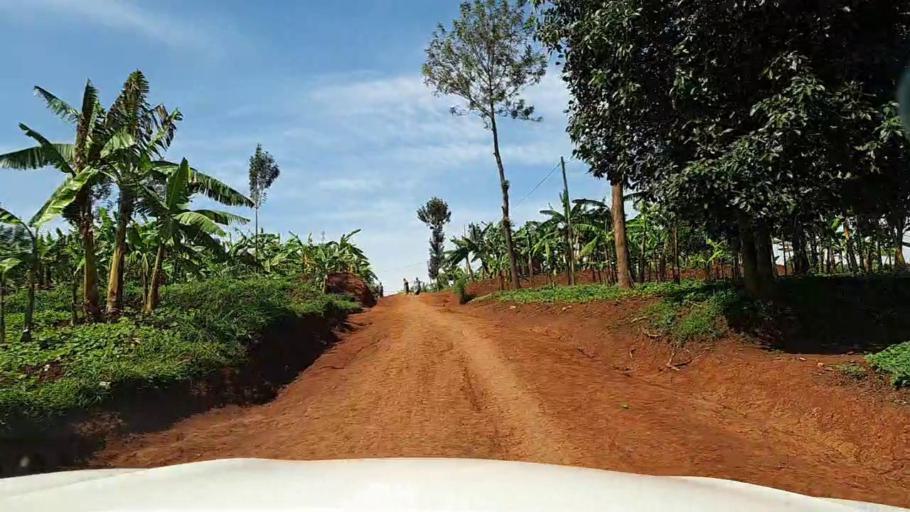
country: RW
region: Southern Province
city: Butare
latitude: -2.7016
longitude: 29.8492
